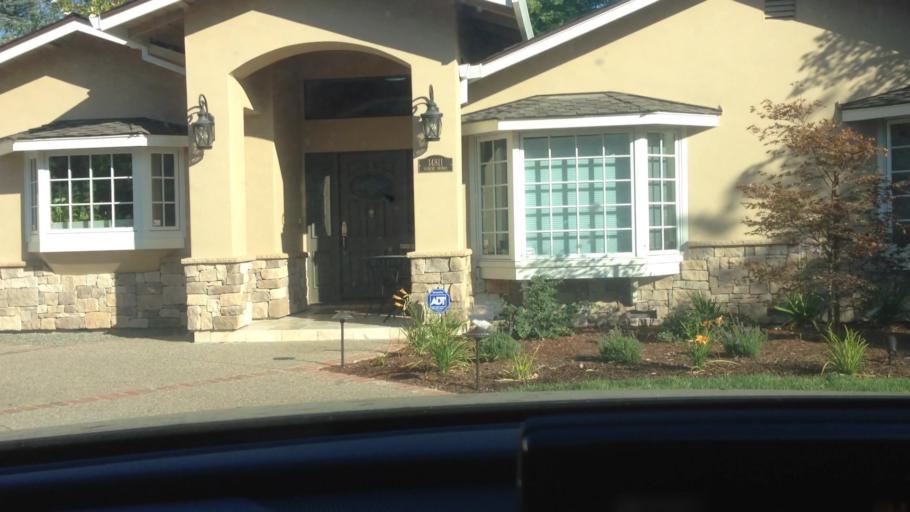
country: US
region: California
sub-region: Santa Clara County
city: Saratoga
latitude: 37.2535
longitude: -122.0313
